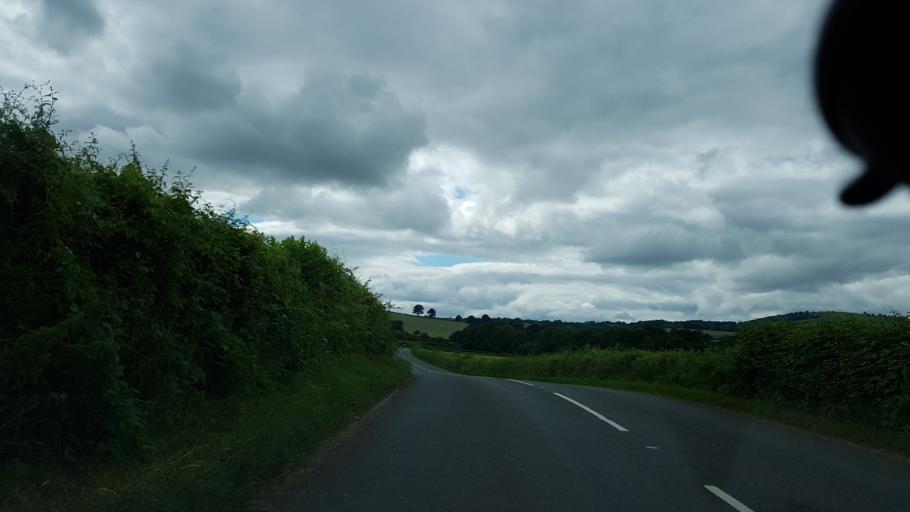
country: GB
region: England
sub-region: Herefordshire
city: Llanrothal
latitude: 51.8775
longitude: -2.8009
